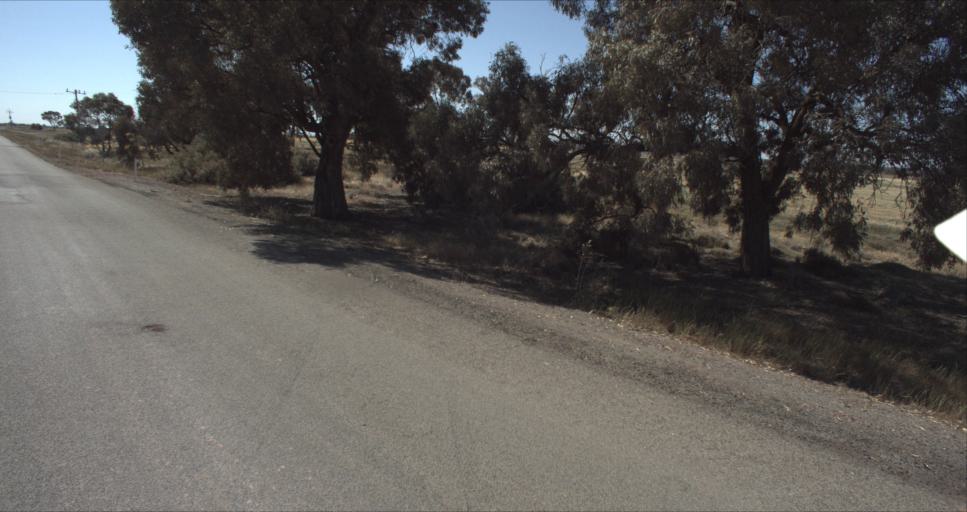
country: AU
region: New South Wales
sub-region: Leeton
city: Leeton
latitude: -34.4997
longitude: 146.3937
